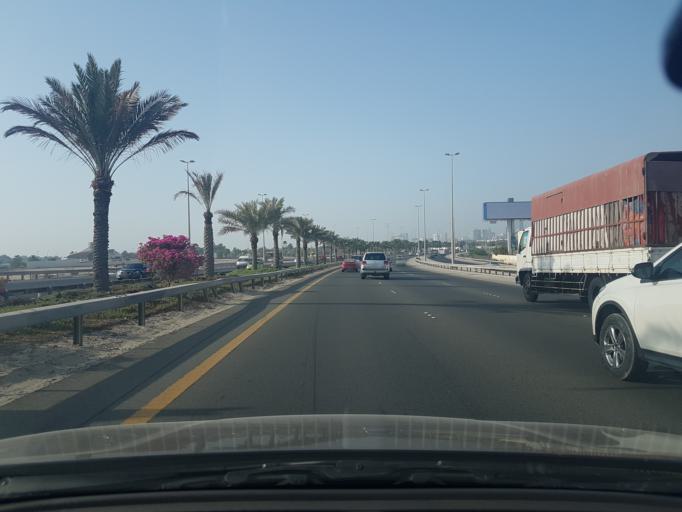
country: BH
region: Manama
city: Jidd Hafs
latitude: 26.2206
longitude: 50.5220
